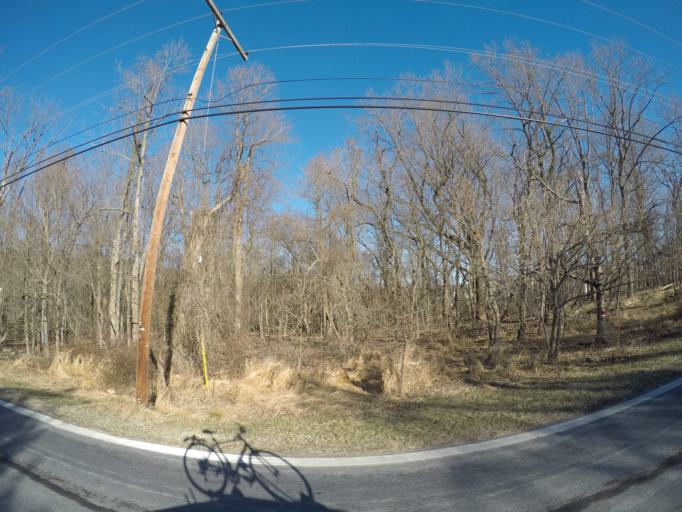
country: US
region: Maryland
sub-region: Howard County
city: Ellicott City
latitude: 39.2589
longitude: -76.7928
